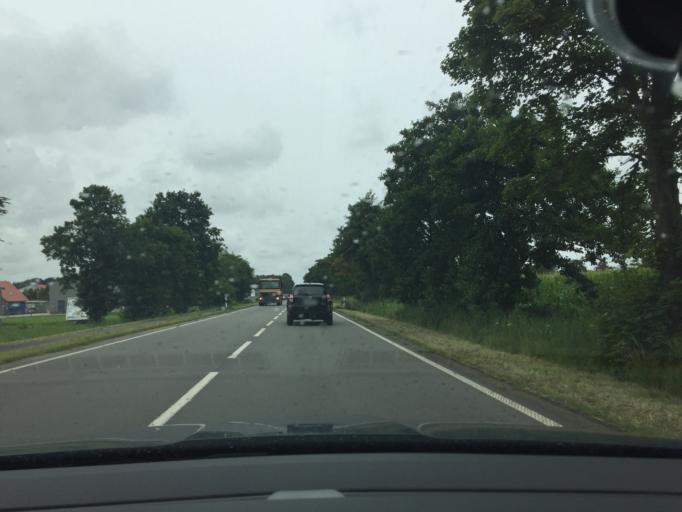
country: DE
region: Lower Saxony
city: Upgant-Schott
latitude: 53.5112
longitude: 7.2882
